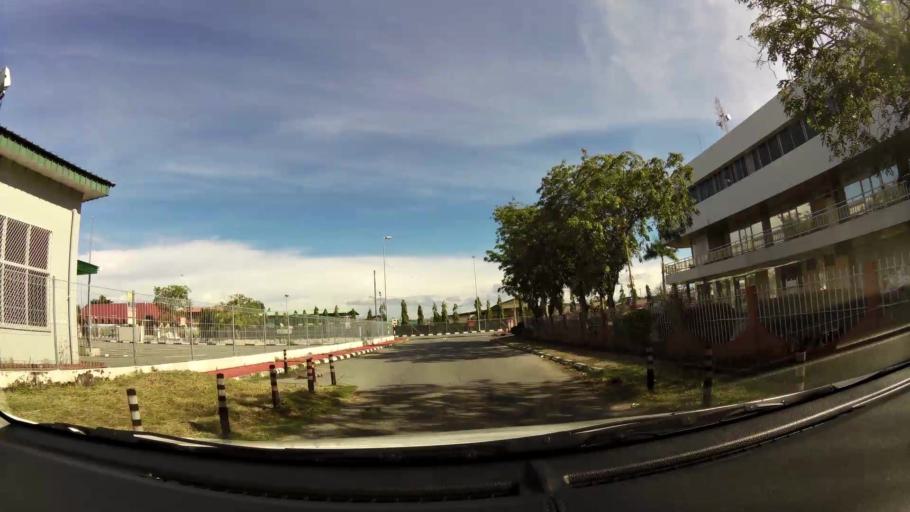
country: BN
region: Belait
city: Kuala Belait
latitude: 4.5777
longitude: 114.2004
